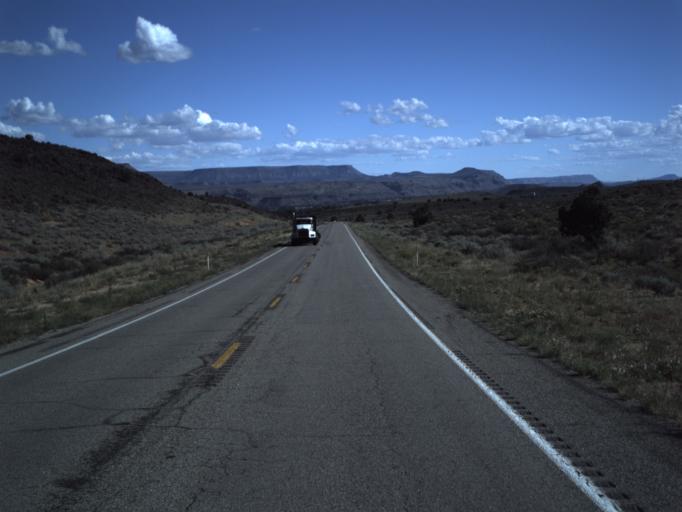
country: US
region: Utah
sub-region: Washington County
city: Toquerville
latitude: 37.2702
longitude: -113.2963
